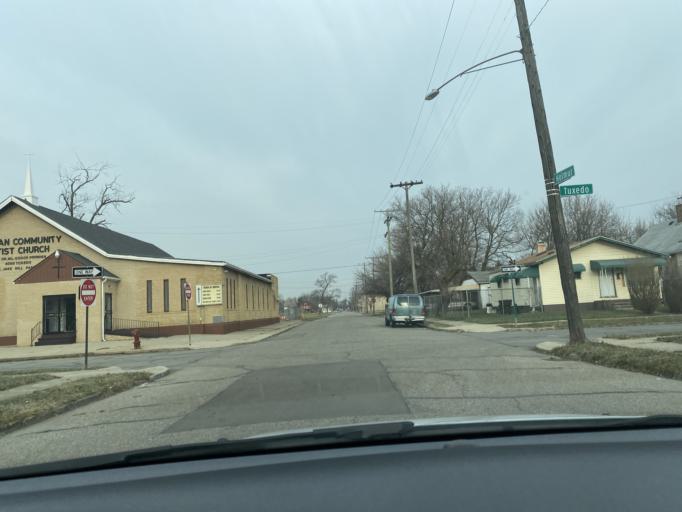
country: US
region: Michigan
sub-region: Wayne County
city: Highland Park
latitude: 42.3792
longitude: -83.1270
